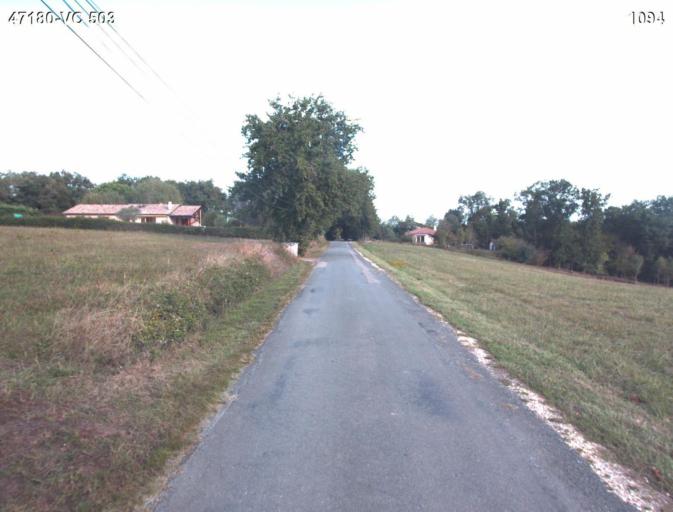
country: FR
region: Aquitaine
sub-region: Departement du Lot-et-Garonne
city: Sainte-Colombe-en-Bruilhois
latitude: 44.1741
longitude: 0.4330
